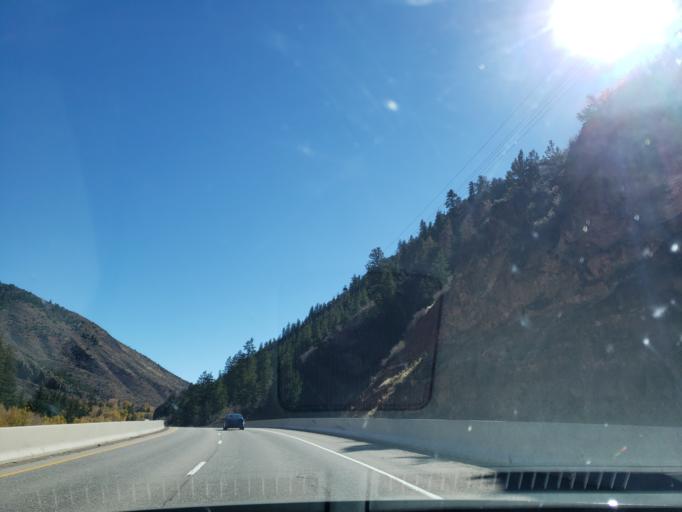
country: US
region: Colorado
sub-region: Eagle County
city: Basalt
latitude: 39.3211
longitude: -106.9460
